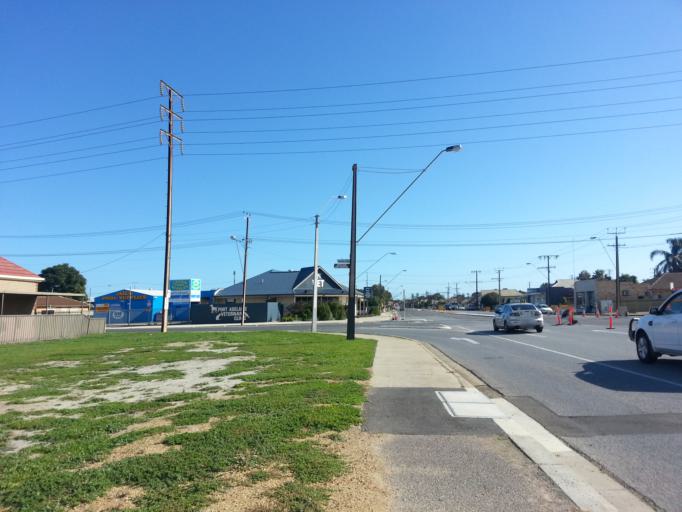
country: AU
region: South Australia
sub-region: Port Adelaide Enfield
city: Birkenhead
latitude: -34.8463
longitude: 138.4919
